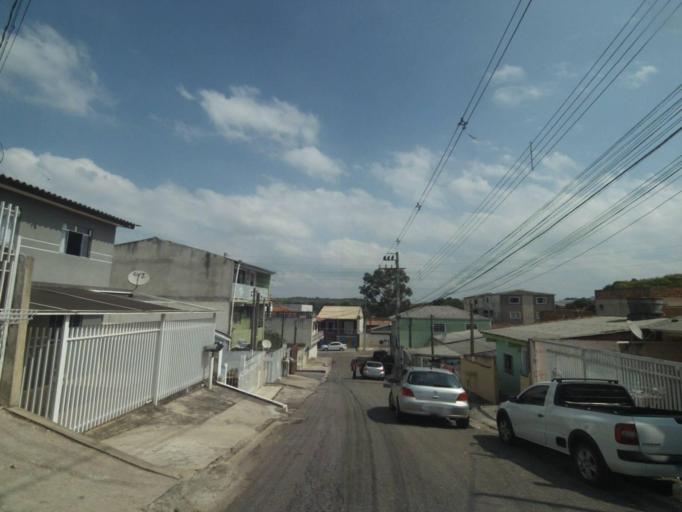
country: BR
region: Parana
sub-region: Curitiba
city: Curitiba
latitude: -25.5012
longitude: -49.3466
